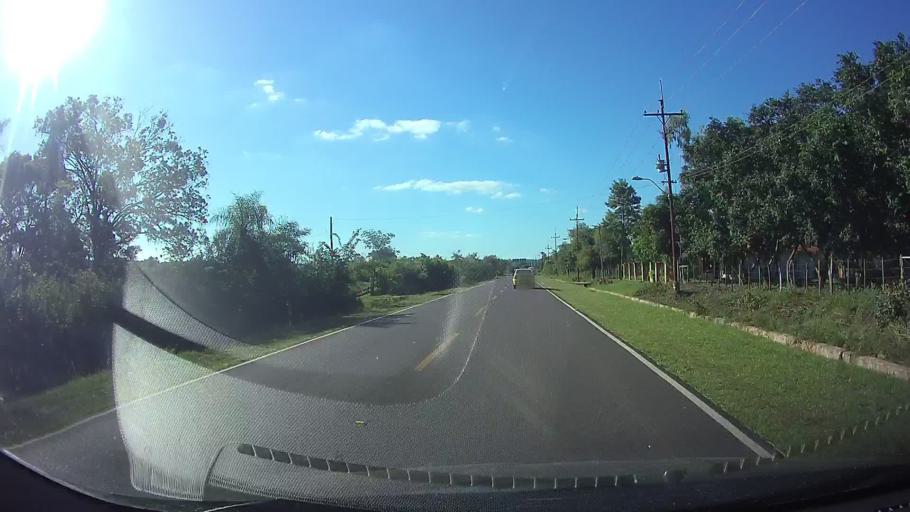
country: PY
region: Cordillera
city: Atyra
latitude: -25.2906
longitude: -57.1677
